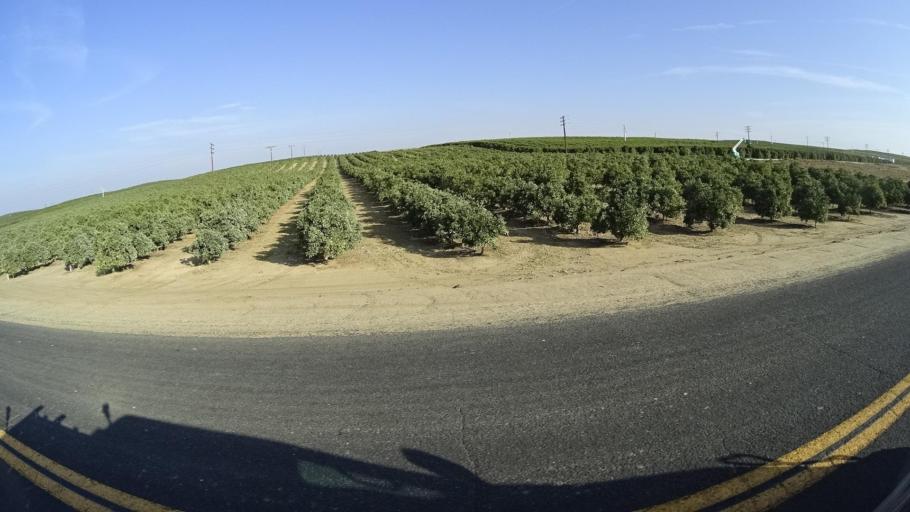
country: US
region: California
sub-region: Tulare County
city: Richgrove
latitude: 35.6597
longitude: -119.0819
